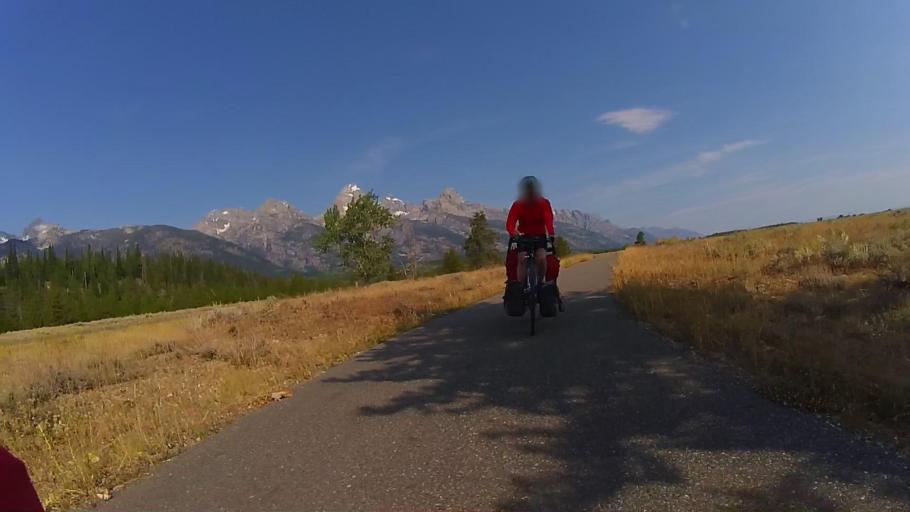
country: US
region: Wyoming
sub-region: Teton County
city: Moose Wilson Road
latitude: 43.6792
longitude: -110.7268
